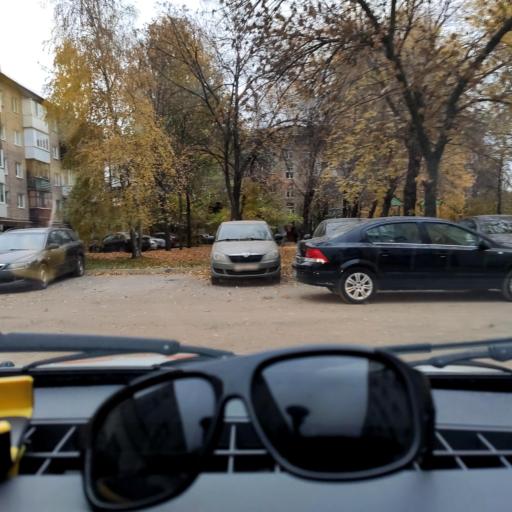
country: RU
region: Bashkortostan
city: Ufa
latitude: 54.7377
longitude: 55.9778
